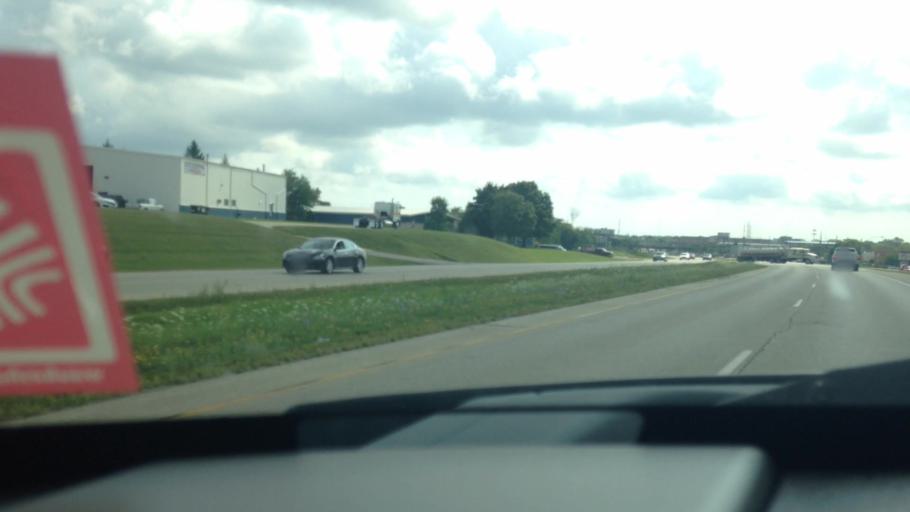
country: US
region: Wisconsin
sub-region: Waukesha County
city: Butler
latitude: 43.1173
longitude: -88.0721
